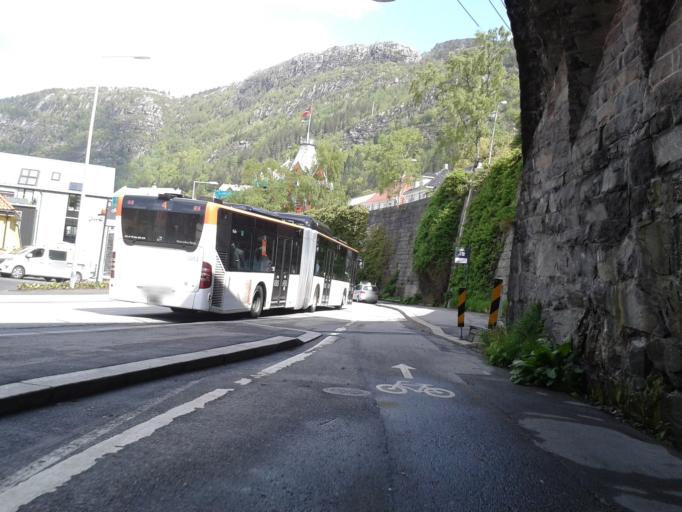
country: NO
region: Hordaland
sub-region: Bergen
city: Bergen
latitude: 60.4038
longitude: 5.3213
